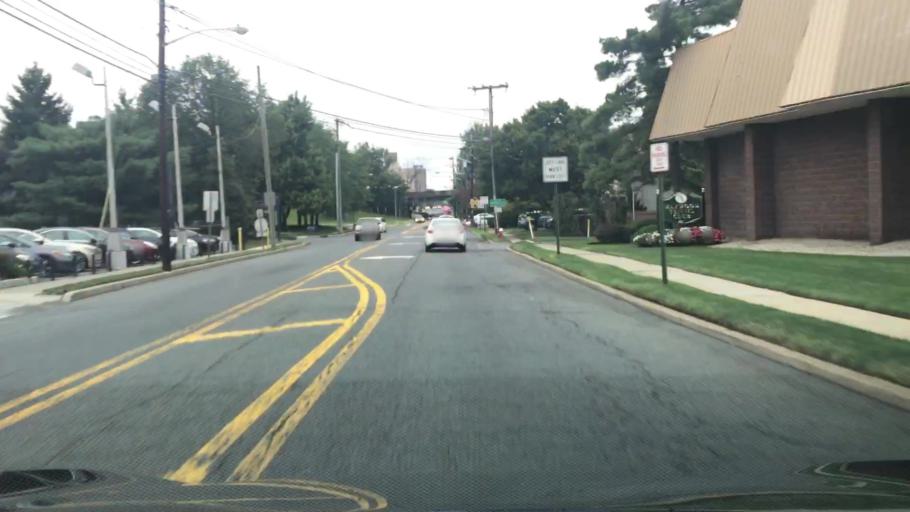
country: US
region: New Jersey
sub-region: Bergen County
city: Rochelle Park
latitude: 40.9068
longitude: -74.0687
